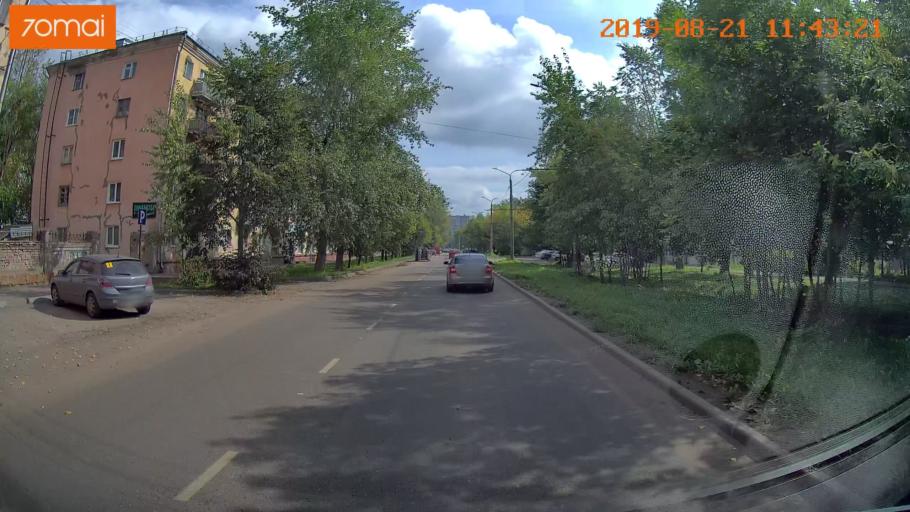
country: RU
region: Ivanovo
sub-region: Gorod Ivanovo
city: Ivanovo
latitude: 57.0009
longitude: 40.9571
